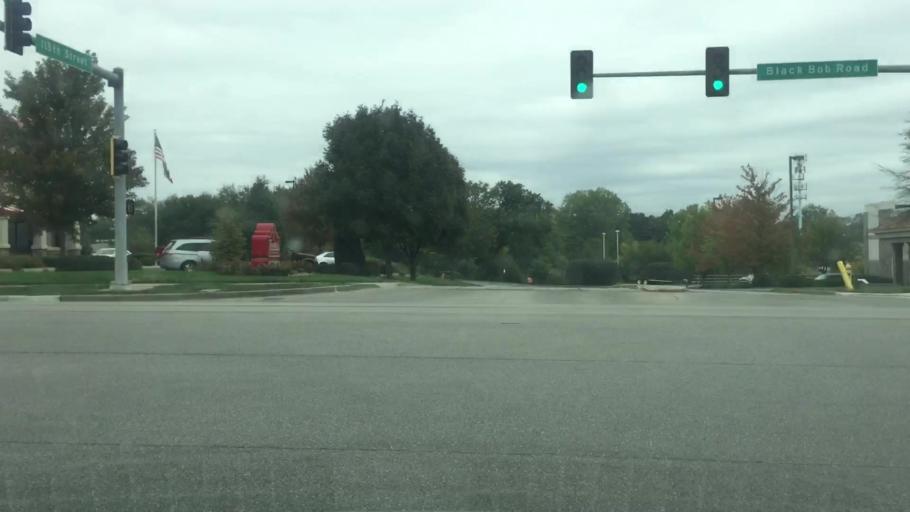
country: US
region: Kansas
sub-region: Johnson County
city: Lenexa
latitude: 38.9143
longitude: -94.7611
